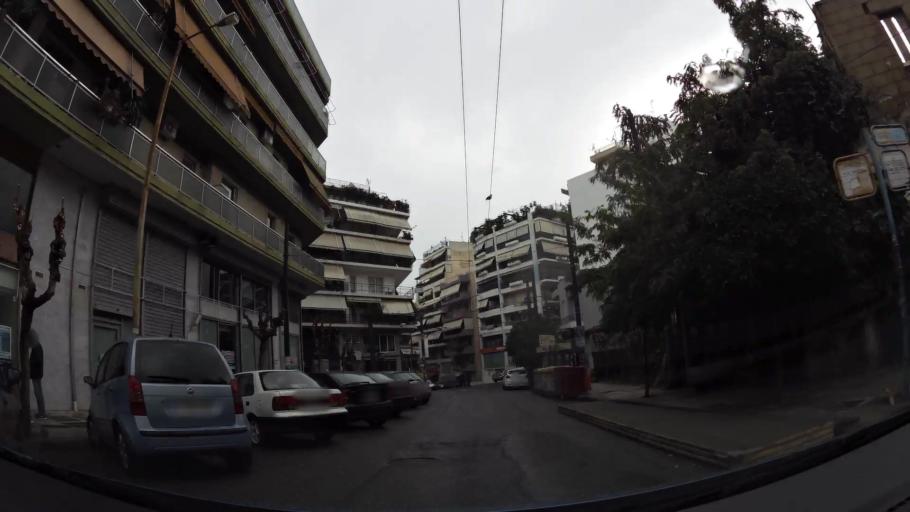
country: GR
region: Attica
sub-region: Nomarchia Athinas
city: Vyronas
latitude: 37.9593
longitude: 23.7554
